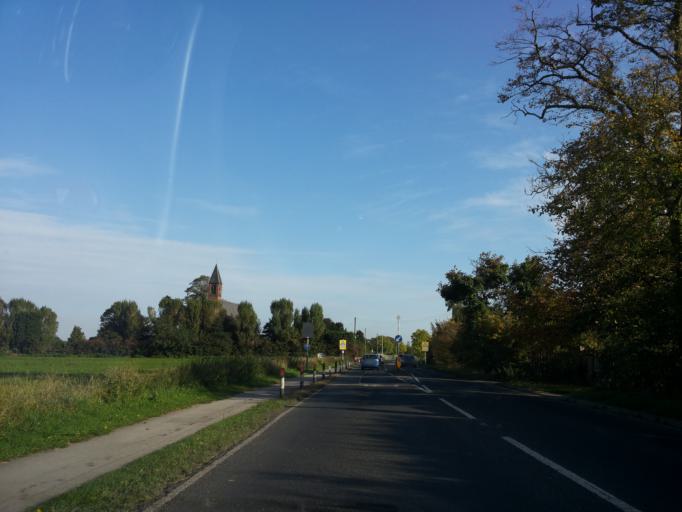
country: GB
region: England
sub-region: East Riding of Yorkshire
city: Snaith
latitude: 53.6869
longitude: -1.0025
